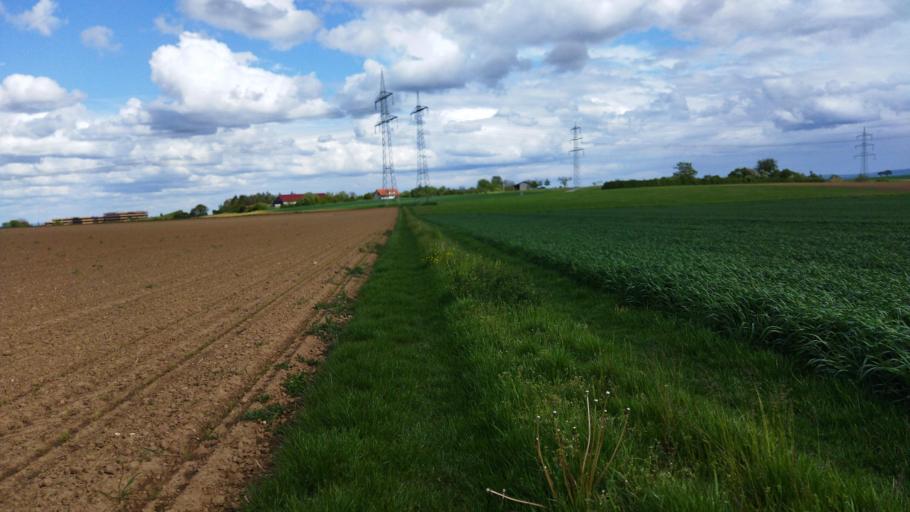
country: DE
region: Baden-Wuerttemberg
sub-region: Regierungsbezirk Stuttgart
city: Bad Wimpfen
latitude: 49.2271
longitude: 9.1298
